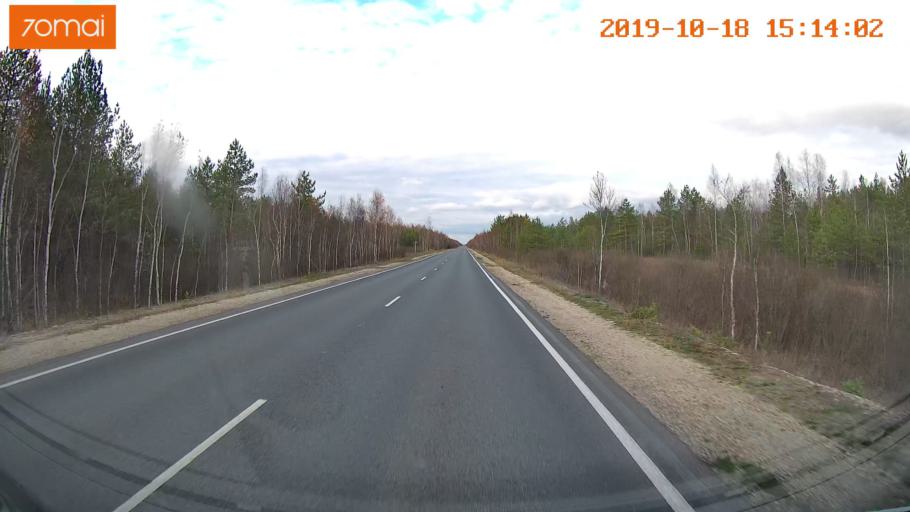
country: RU
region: Vladimir
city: Gus'-Khrustal'nyy
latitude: 55.5961
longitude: 40.7194
